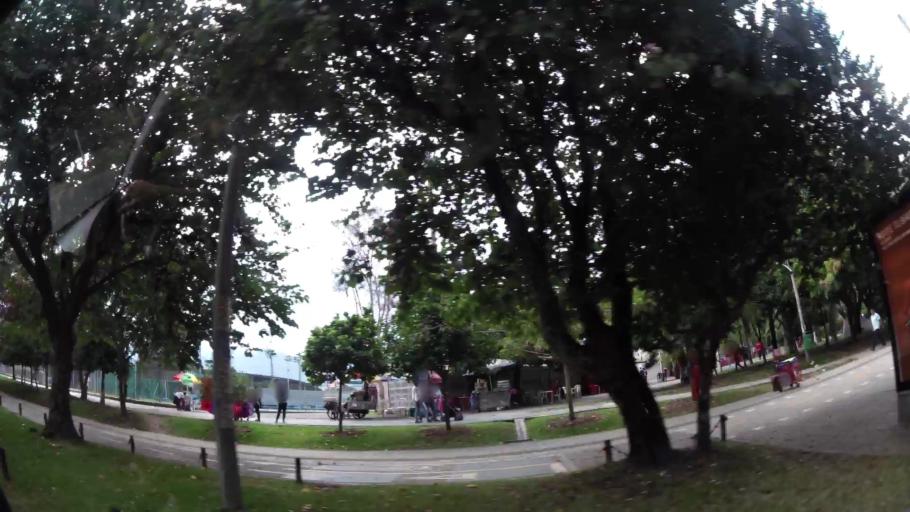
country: CO
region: Antioquia
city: Medellin
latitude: 6.2575
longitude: -75.5866
